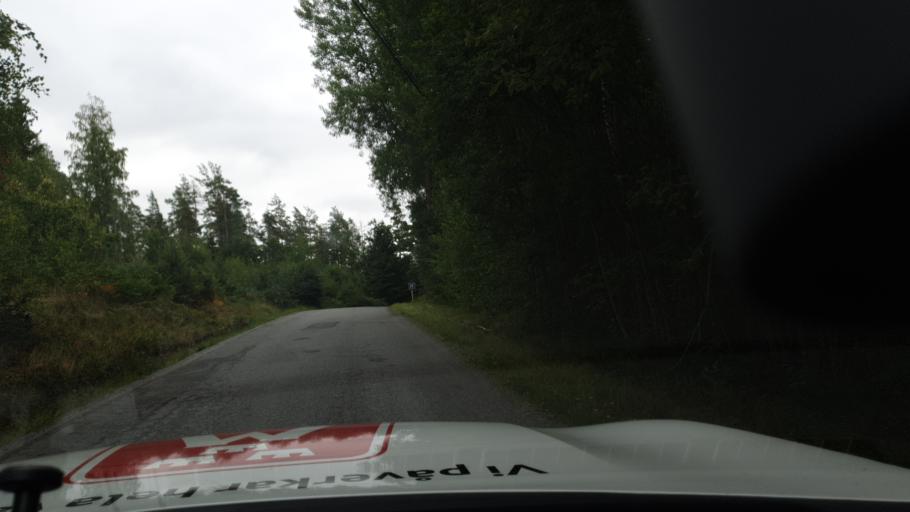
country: SE
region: Soedermanland
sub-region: Strangnas Kommun
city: Akers Styckebruk
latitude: 59.1813
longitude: 17.1566
